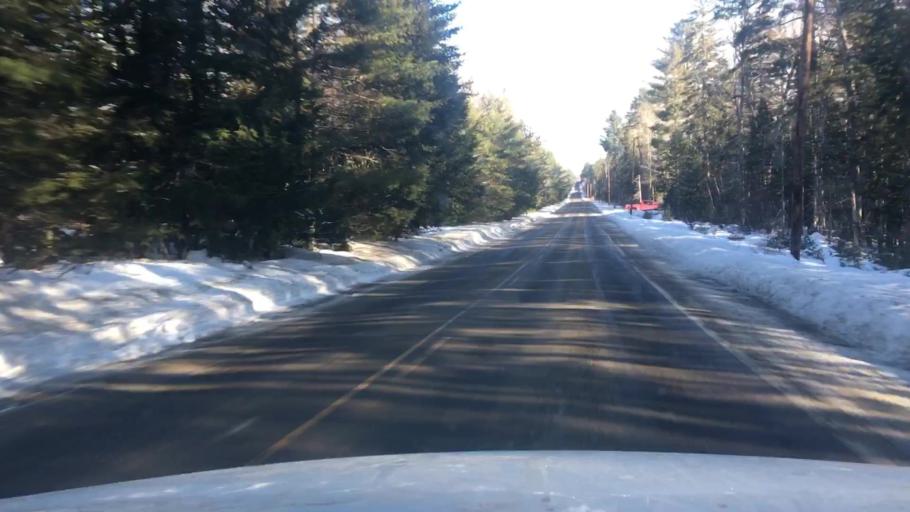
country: US
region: Maine
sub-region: Hancock County
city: Ellsworth
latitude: 44.6673
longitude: -68.3552
